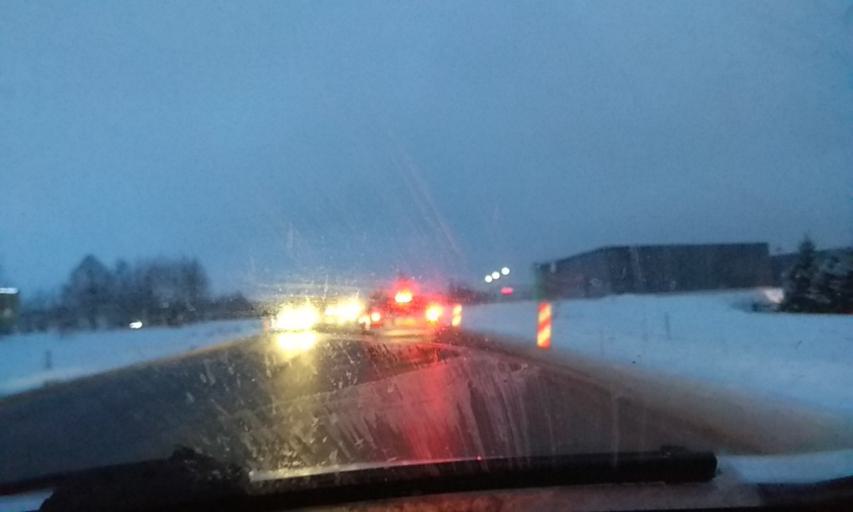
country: LT
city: Ramuciai
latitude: 54.9069
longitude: 24.0302
